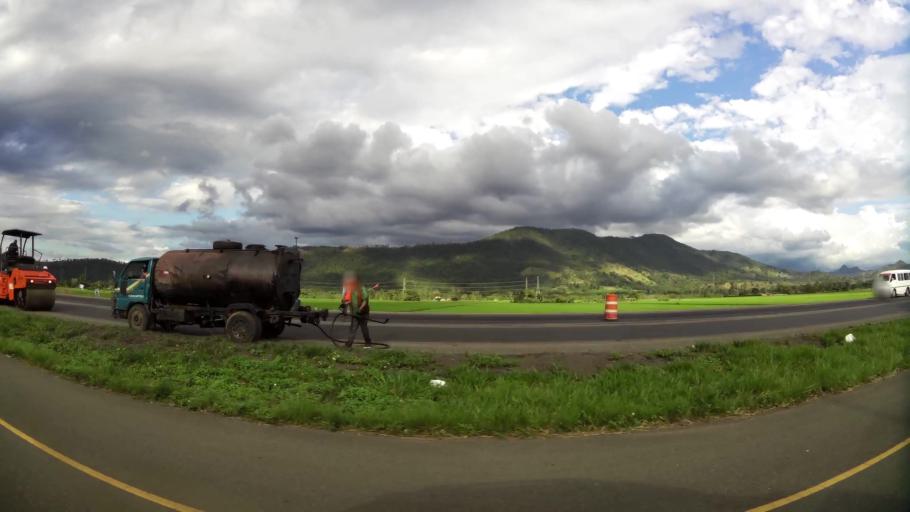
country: DO
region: Monsenor Nouel
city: Bonao
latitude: 18.8982
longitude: -70.3698
